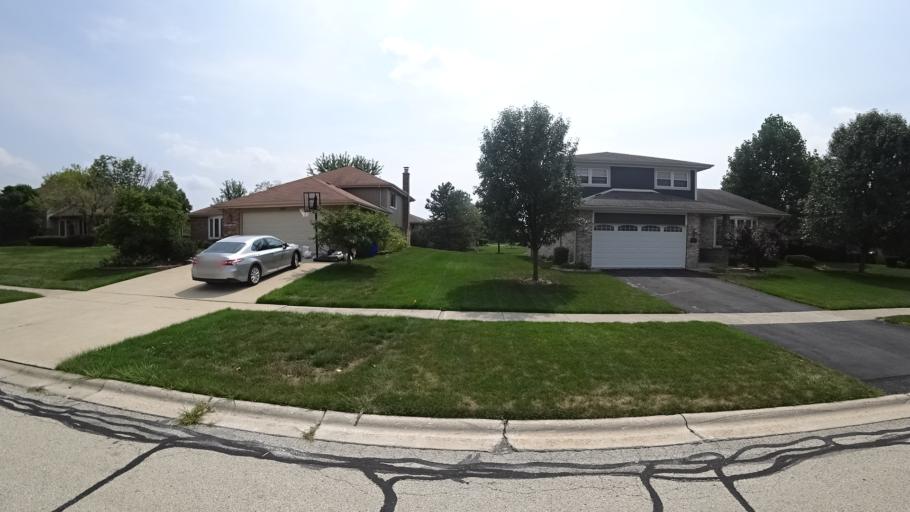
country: US
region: Illinois
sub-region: Will County
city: Goodings Grove
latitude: 41.6289
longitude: -87.9043
